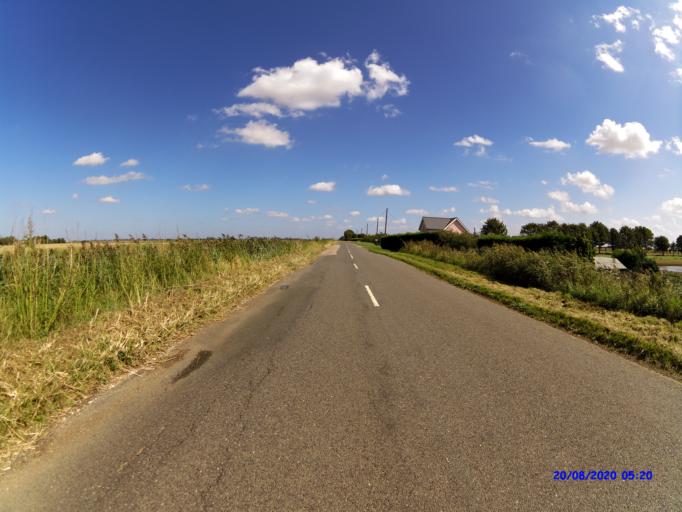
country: GB
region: England
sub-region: Cambridgeshire
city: Whittlesey
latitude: 52.5274
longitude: -0.1056
